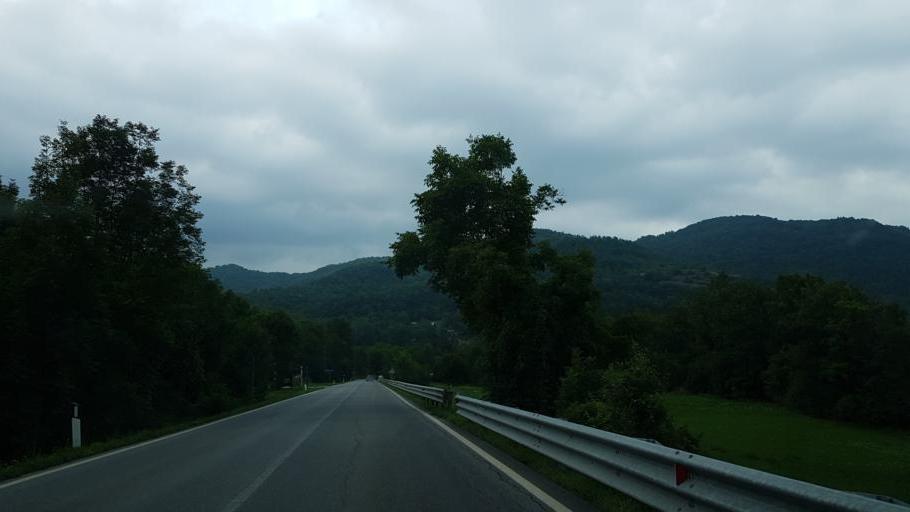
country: IT
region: Piedmont
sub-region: Provincia di Cuneo
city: Moiola
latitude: 44.3271
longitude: 7.3967
